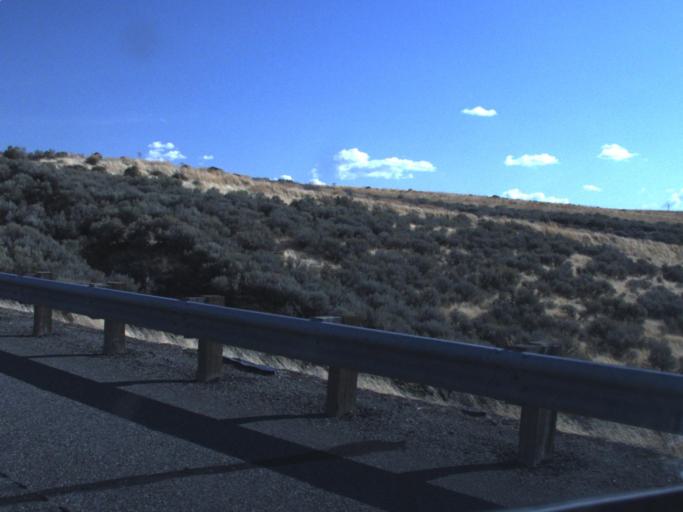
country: US
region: Washington
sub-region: Franklin County
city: West Pasco
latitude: 46.1770
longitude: -119.2329
